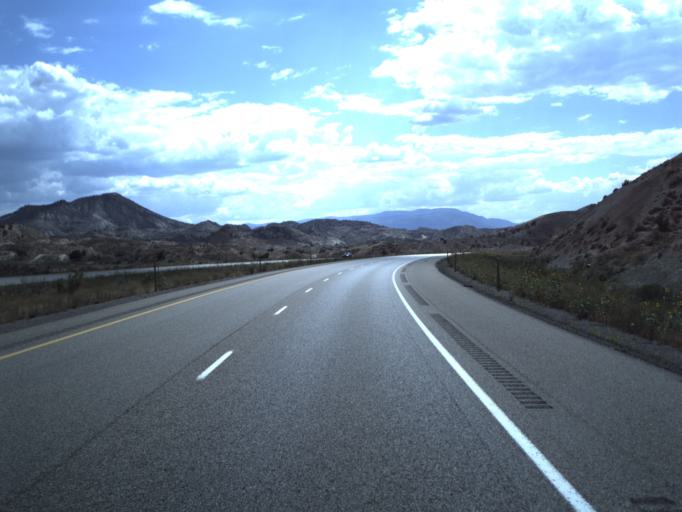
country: US
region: Utah
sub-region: Sevier County
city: Aurora
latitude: 38.8942
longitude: -111.9058
